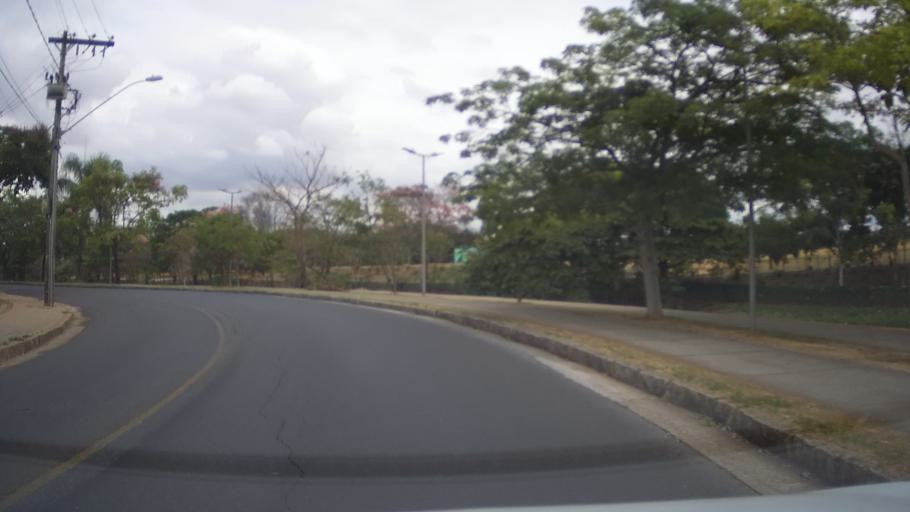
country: BR
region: Minas Gerais
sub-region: Belo Horizonte
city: Belo Horizonte
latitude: -19.8539
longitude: -43.9942
